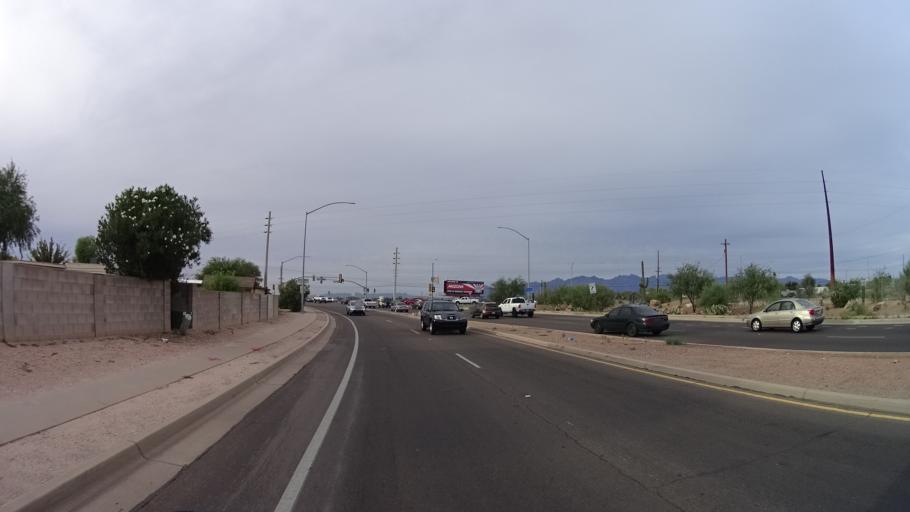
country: US
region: Arizona
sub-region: Pima County
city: South Tucson
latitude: 32.1624
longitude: -110.9351
